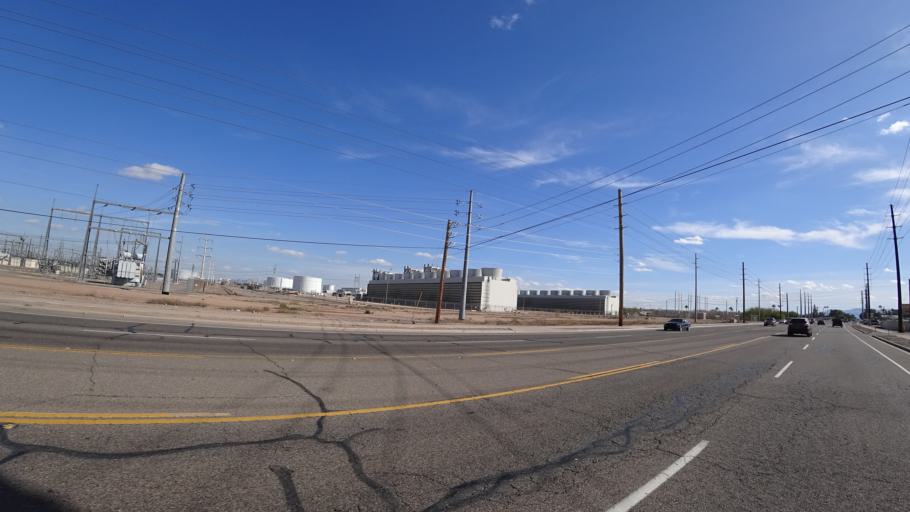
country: US
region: Arizona
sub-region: Maricopa County
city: Peoria
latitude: 33.5563
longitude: -112.2205
